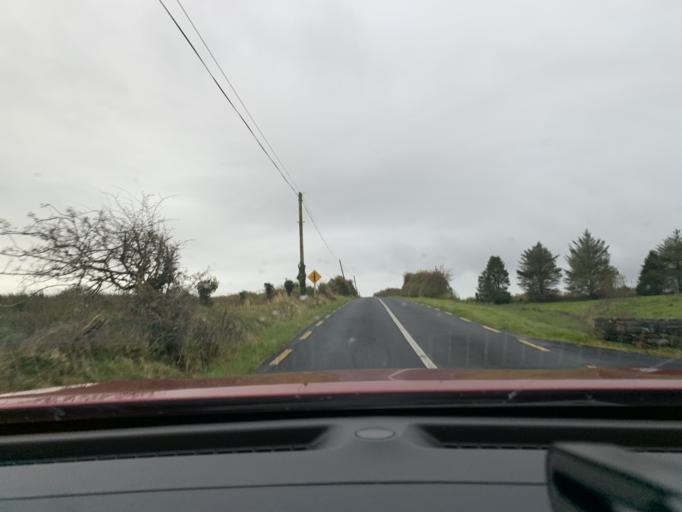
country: IE
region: Connaught
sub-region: Roscommon
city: Ballaghaderreen
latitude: 53.9563
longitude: -8.5431
